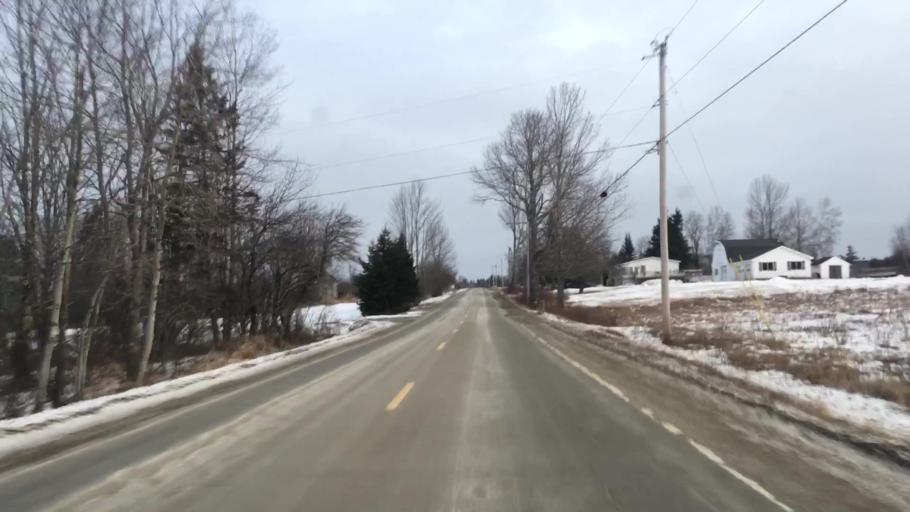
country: US
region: Maine
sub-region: Hancock County
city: Franklin
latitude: 44.7145
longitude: -68.3373
